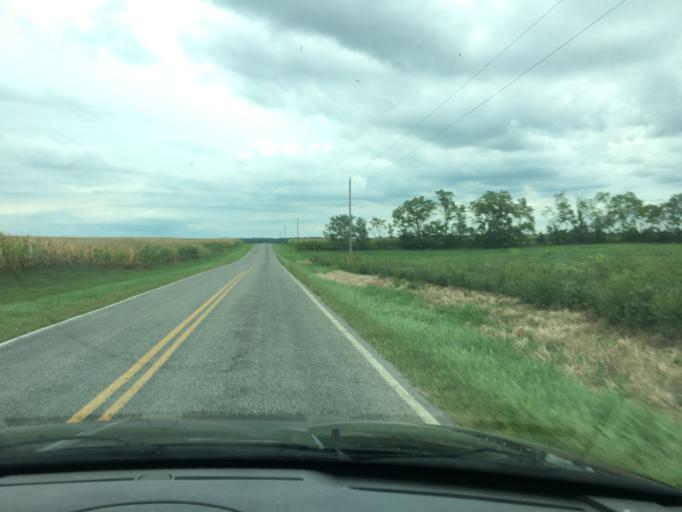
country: US
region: Ohio
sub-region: Logan County
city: West Liberty
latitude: 40.1920
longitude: -83.7534
